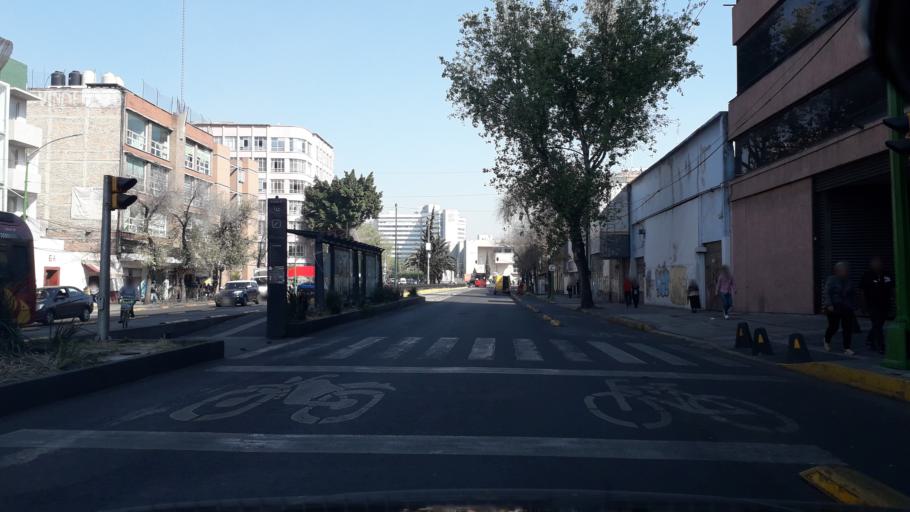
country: MX
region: Mexico City
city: Cuauhtemoc
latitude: 19.4393
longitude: -99.1531
